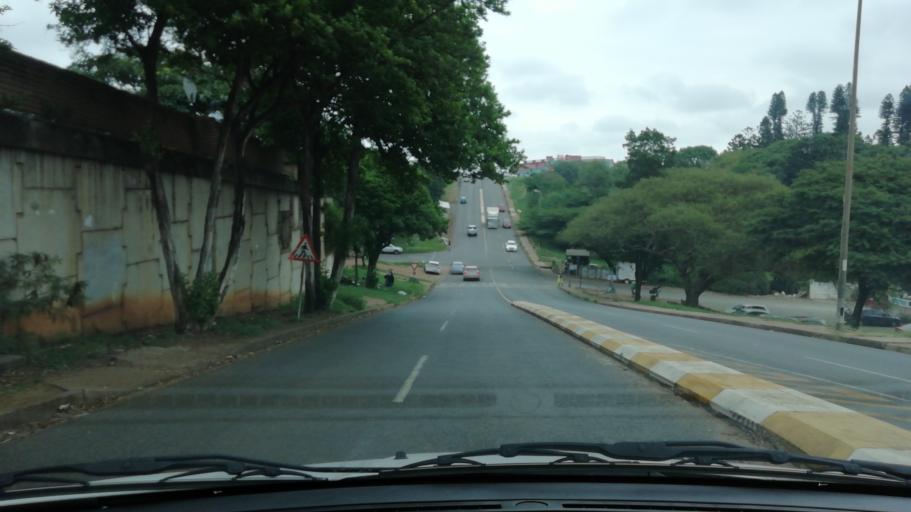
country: ZA
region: KwaZulu-Natal
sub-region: uThungulu District Municipality
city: Empangeni
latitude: -28.7427
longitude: 31.8871
